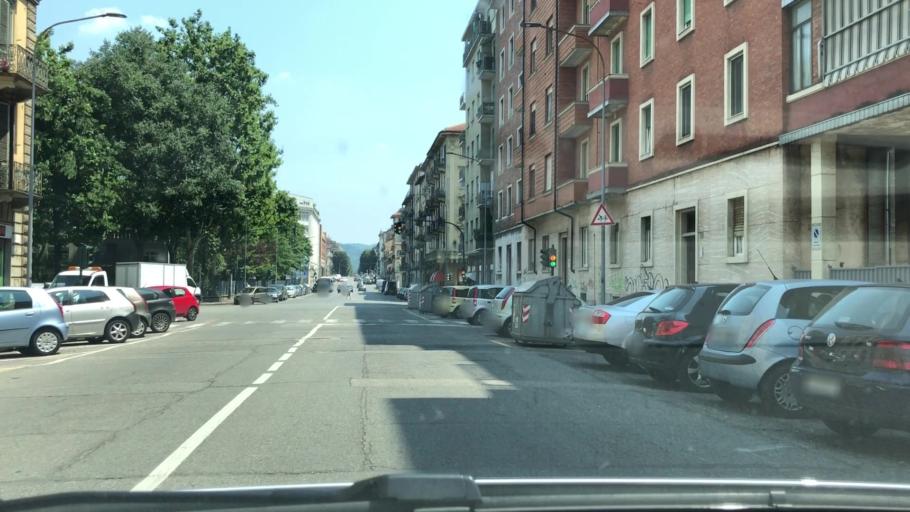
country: IT
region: Piedmont
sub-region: Provincia di Torino
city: Turin
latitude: 45.0845
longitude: 7.6828
